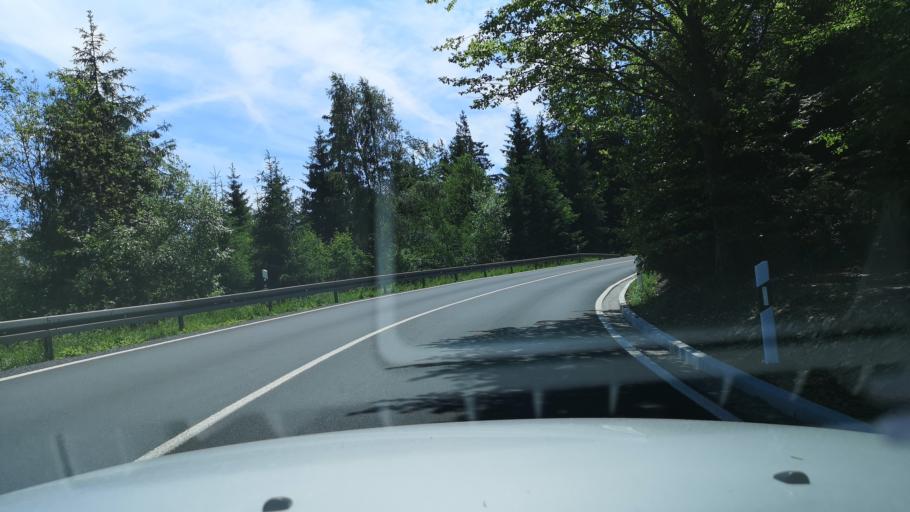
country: DE
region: Thuringia
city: Piesau
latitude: 50.5039
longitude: 11.2329
